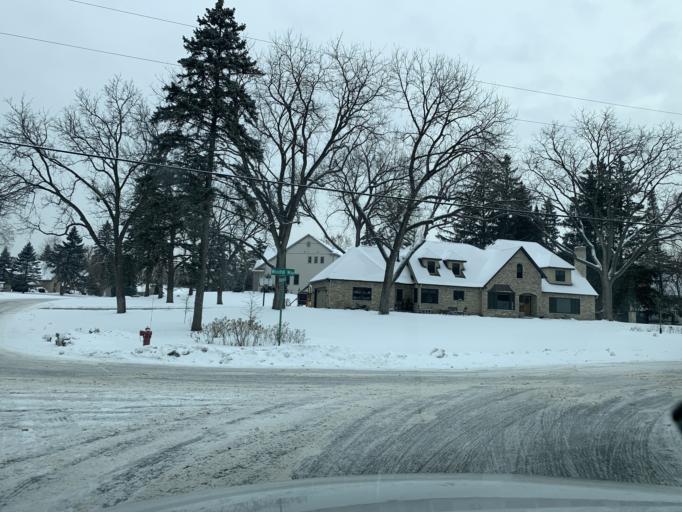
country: US
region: Minnesota
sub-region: Hennepin County
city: Edina
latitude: 44.9145
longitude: -93.3492
